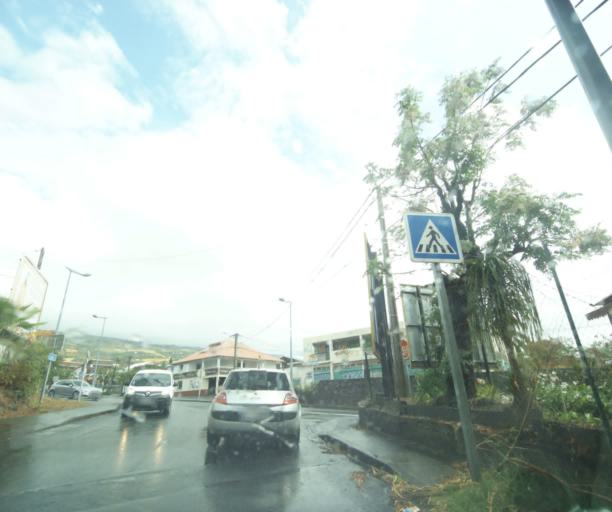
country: RE
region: Reunion
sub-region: Reunion
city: La Possession
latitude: -20.9773
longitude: 55.3286
